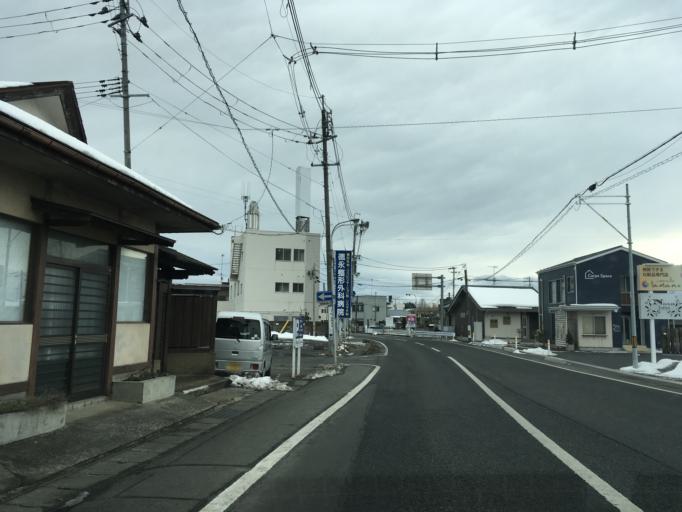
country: JP
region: Miyagi
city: Furukawa
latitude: 38.5748
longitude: 140.9596
